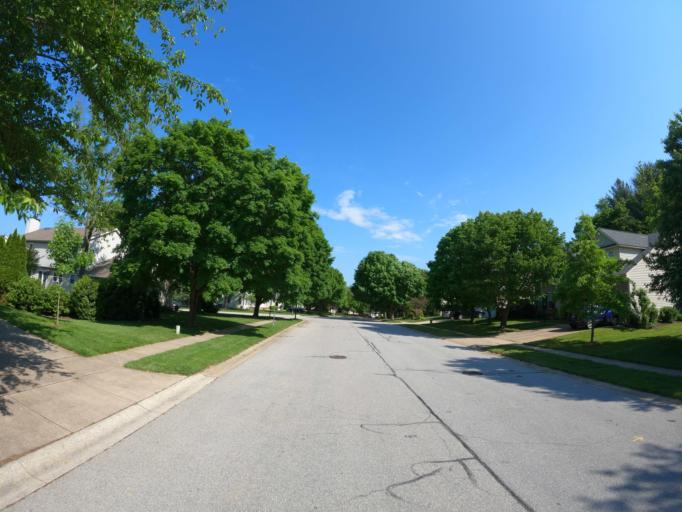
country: US
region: Maryland
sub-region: Howard County
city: Riverside
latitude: 39.1952
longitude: -76.9118
